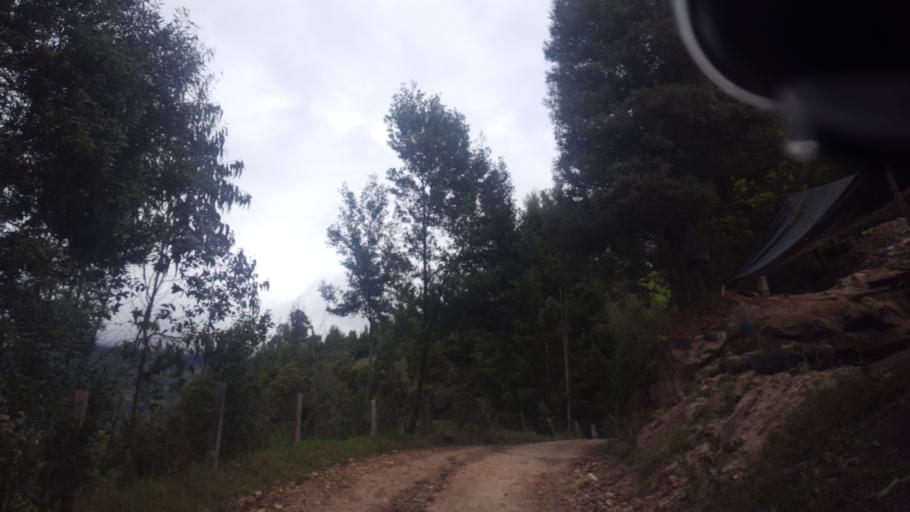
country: CO
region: Boyaca
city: Cerinza
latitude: 5.9833
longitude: -72.9445
